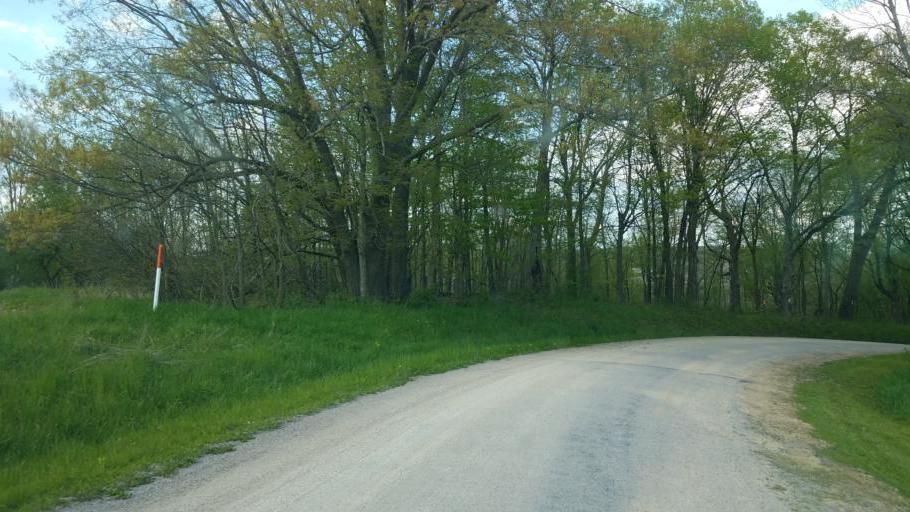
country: US
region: Wisconsin
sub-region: Vernon County
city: Hillsboro
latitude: 43.6539
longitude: -90.3729
